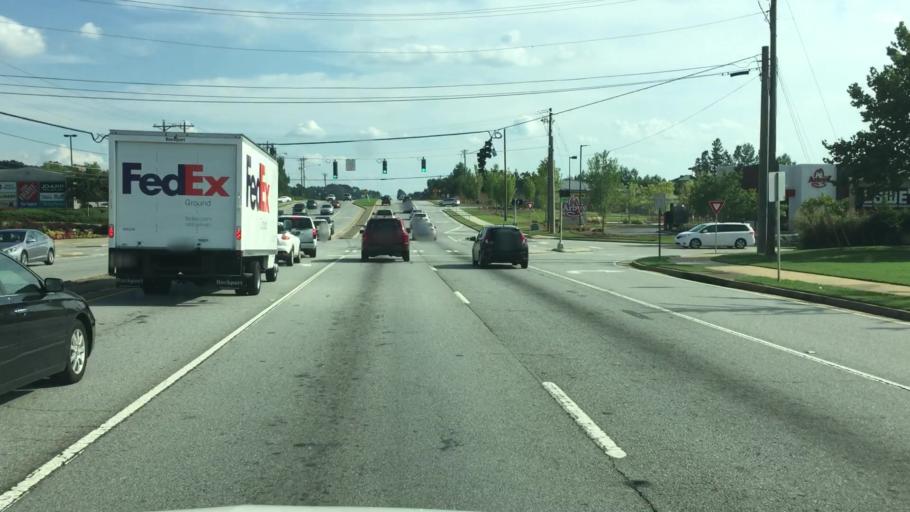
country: US
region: Georgia
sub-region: Gwinnett County
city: Snellville
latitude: 33.8837
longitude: -84.0108
